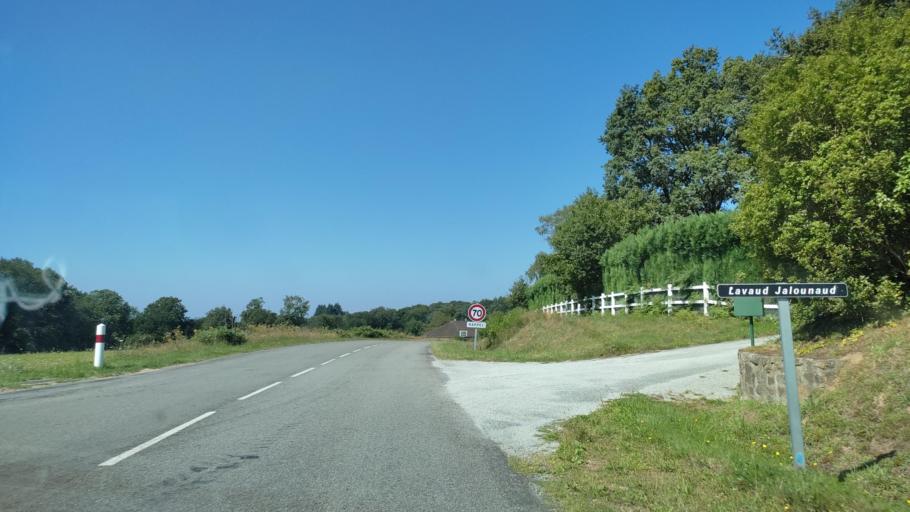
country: FR
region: Limousin
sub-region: Departement de la Haute-Vienne
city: Razes
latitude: 46.0327
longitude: 1.3310
